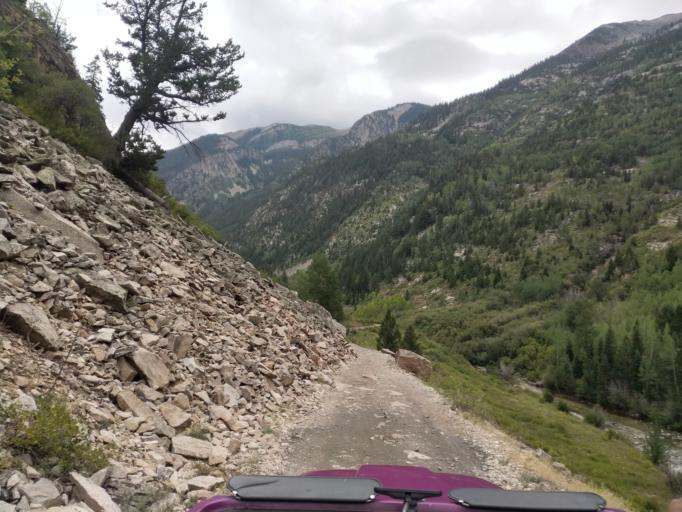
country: US
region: Colorado
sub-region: Gunnison County
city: Crested Butte
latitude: 39.0589
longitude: -107.1373
